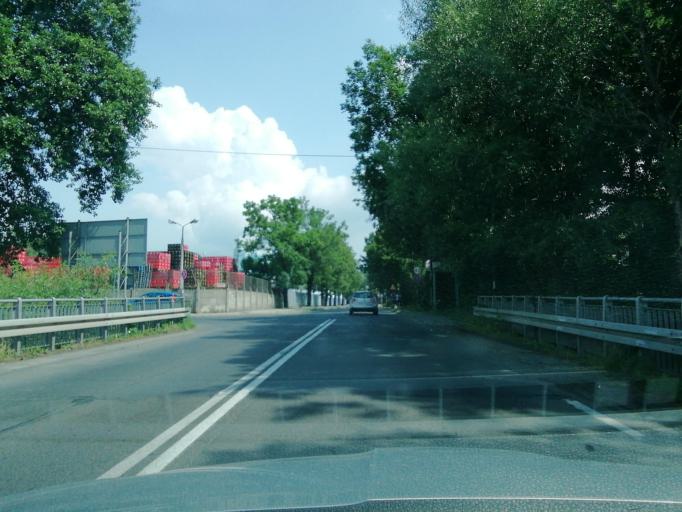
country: PL
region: Silesian Voivodeship
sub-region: Powiat zywiecki
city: Wieprz
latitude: 49.6589
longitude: 19.1722
